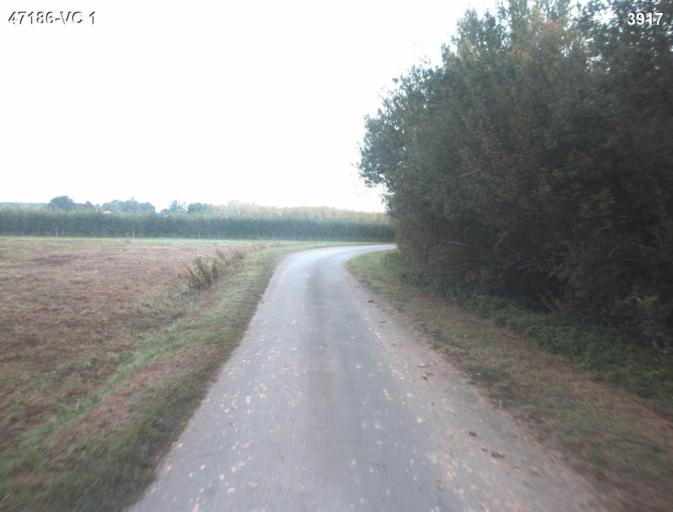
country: FR
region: Aquitaine
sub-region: Departement du Lot-et-Garonne
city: Port-Sainte-Marie
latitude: 44.2206
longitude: 0.4428
